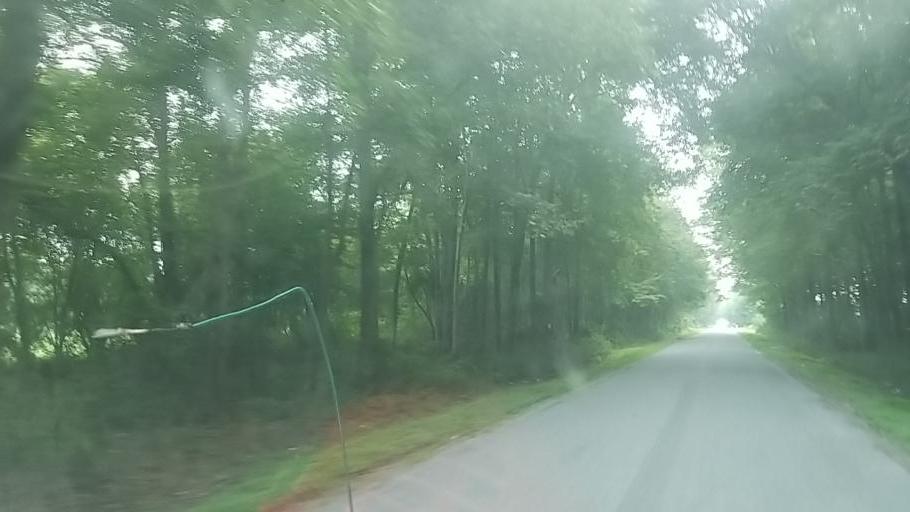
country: US
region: Maryland
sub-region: Wicomico County
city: Pittsville
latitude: 38.4521
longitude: -75.3865
